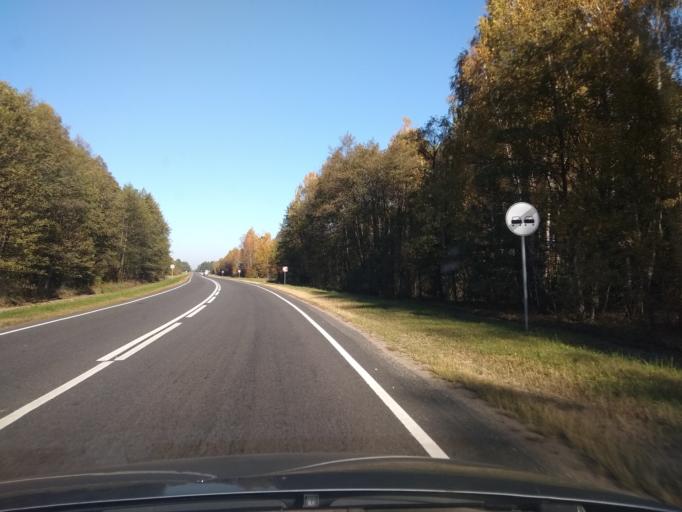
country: BY
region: Brest
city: Kobryn
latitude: 52.0658
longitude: 24.2844
